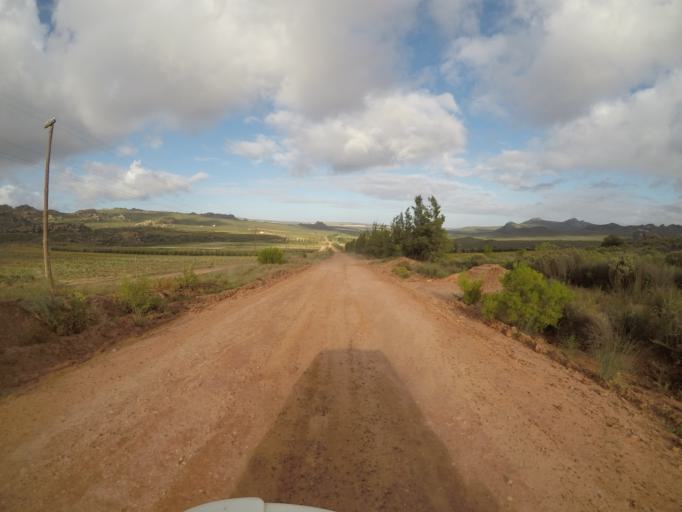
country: ZA
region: Western Cape
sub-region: West Coast District Municipality
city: Clanwilliam
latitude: -32.3443
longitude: 18.7551
